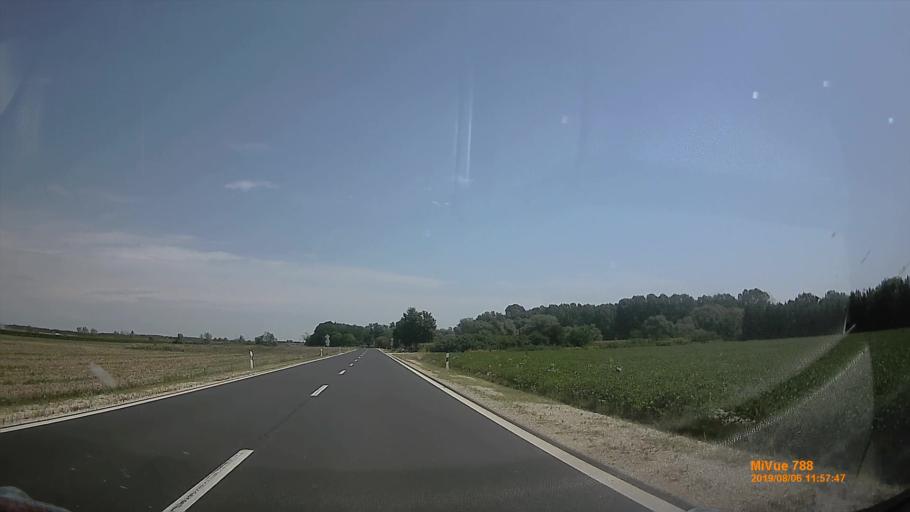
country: HU
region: Vas
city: Vasvar
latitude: 47.0615
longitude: 16.7155
